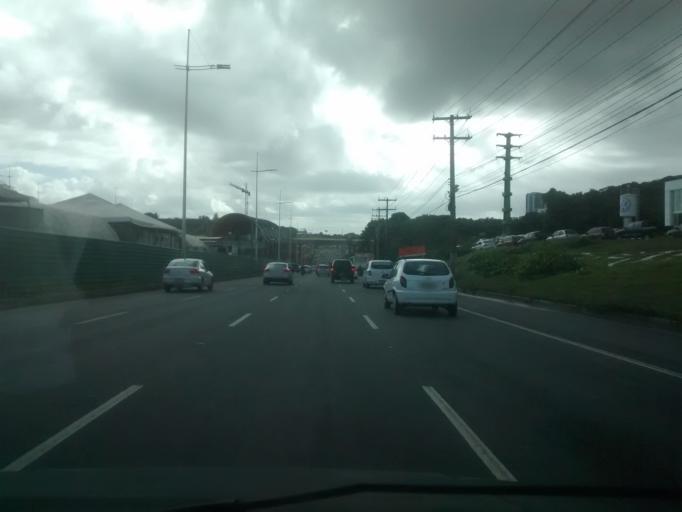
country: BR
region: Bahia
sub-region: Salvador
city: Salvador
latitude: -12.9487
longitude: -38.4233
